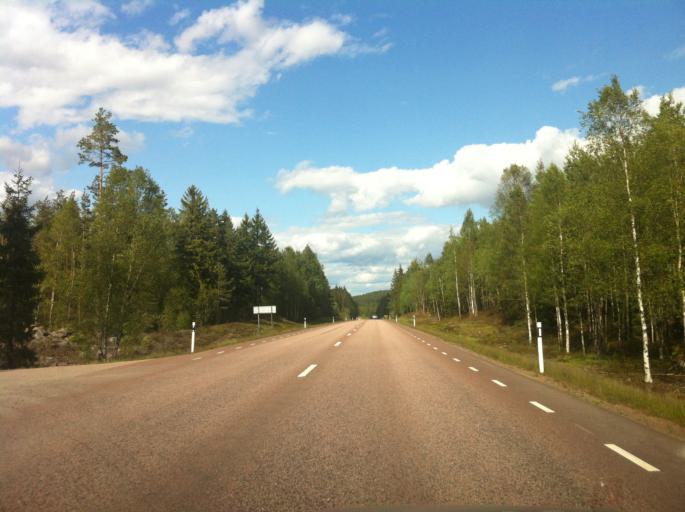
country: SE
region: Vaermland
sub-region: Kristinehamns Kommun
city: Kristinehamn
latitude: 59.3554
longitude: 14.1458
